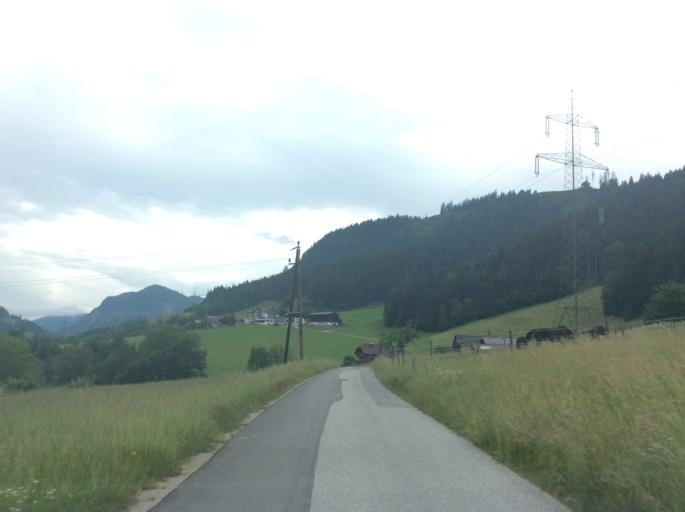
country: AT
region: Styria
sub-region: Politischer Bezirk Liezen
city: Schladming
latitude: 47.3902
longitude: 13.6460
